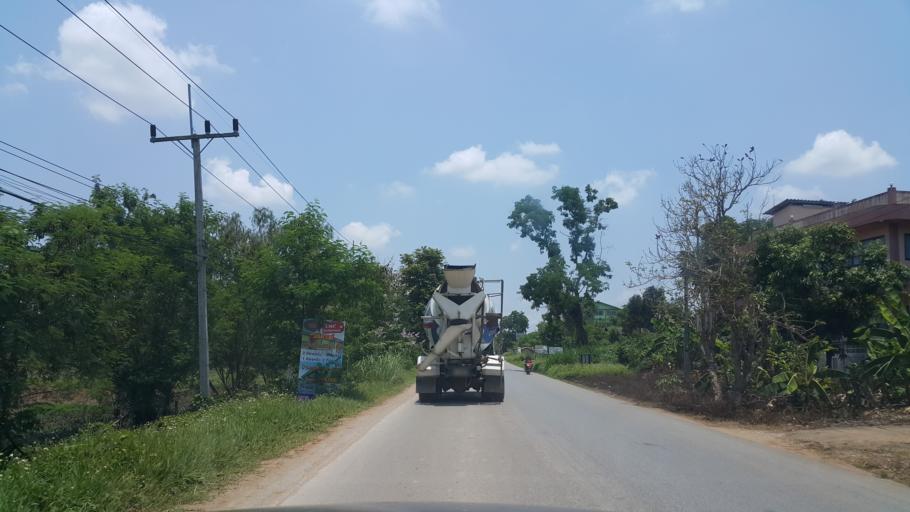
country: TH
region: Chiang Rai
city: Chiang Rai
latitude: 19.9375
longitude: 99.8099
